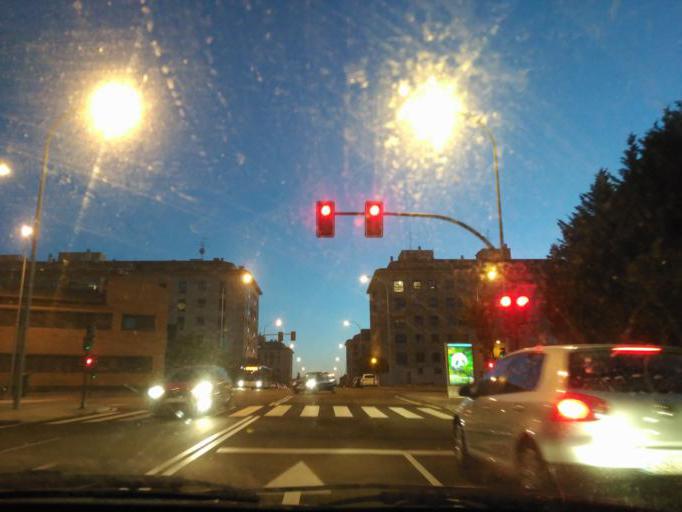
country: ES
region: Castille and Leon
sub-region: Provincia de Salamanca
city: Salamanca
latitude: 40.9834
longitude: -5.6673
